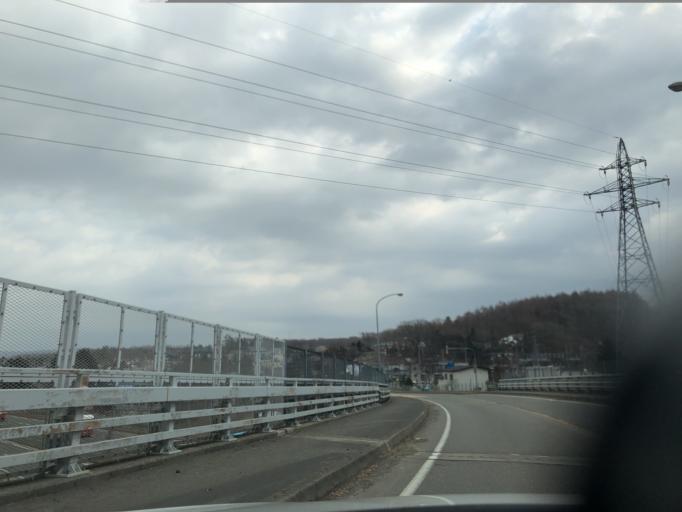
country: JP
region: Hokkaido
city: Chitose
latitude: 42.7622
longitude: 141.8098
